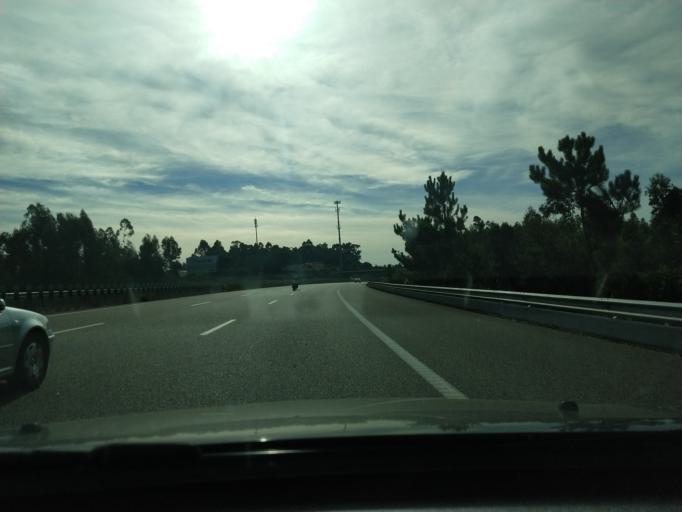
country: PT
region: Aveiro
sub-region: Santa Maria da Feira
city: Feira
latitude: 40.8840
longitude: -8.5633
